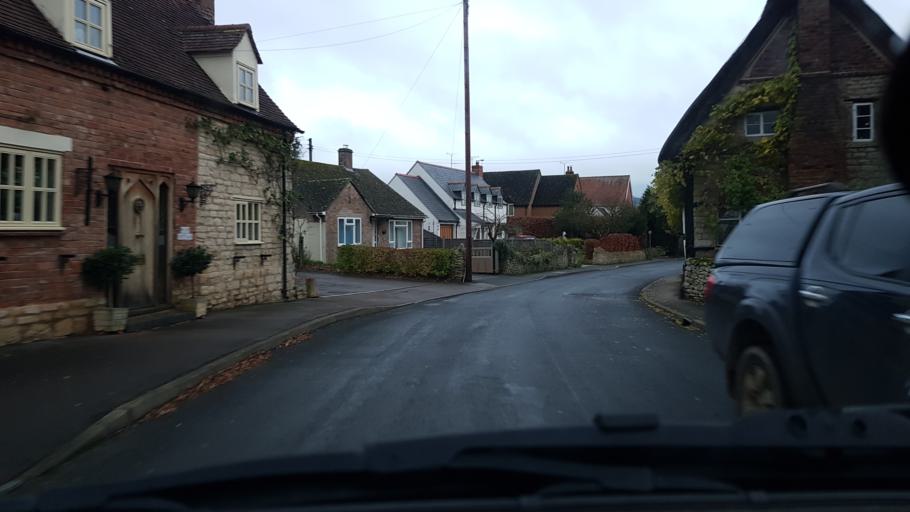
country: GB
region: England
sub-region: Gloucestershire
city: Winchcombe
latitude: 51.9980
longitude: -1.9992
